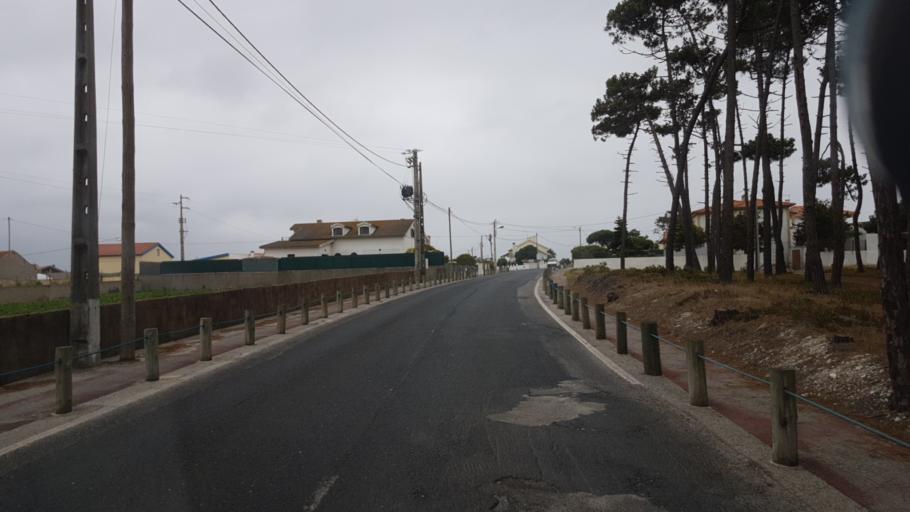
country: PT
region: Lisbon
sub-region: Torres Vedras
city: Silveira
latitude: 39.1541
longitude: -9.3609
